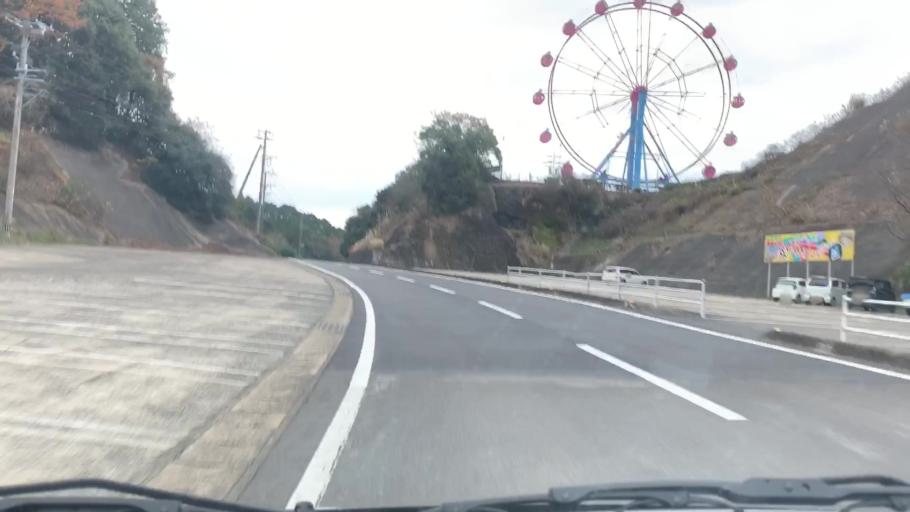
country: JP
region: Saga Prefecture
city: Ureshinomachi-shimojuku
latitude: 33.1308
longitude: 129.9751
